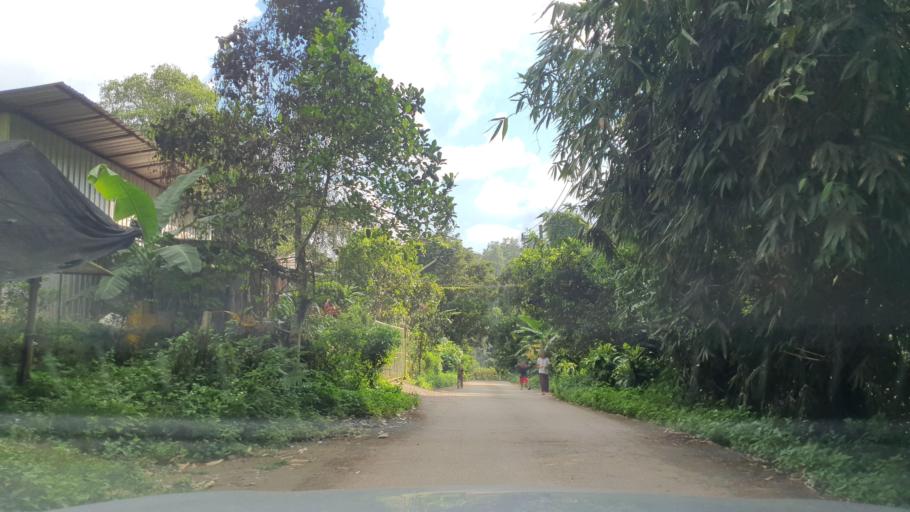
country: TH
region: Chiang Mai
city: Mae On
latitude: 18.9400
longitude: 99.3094
